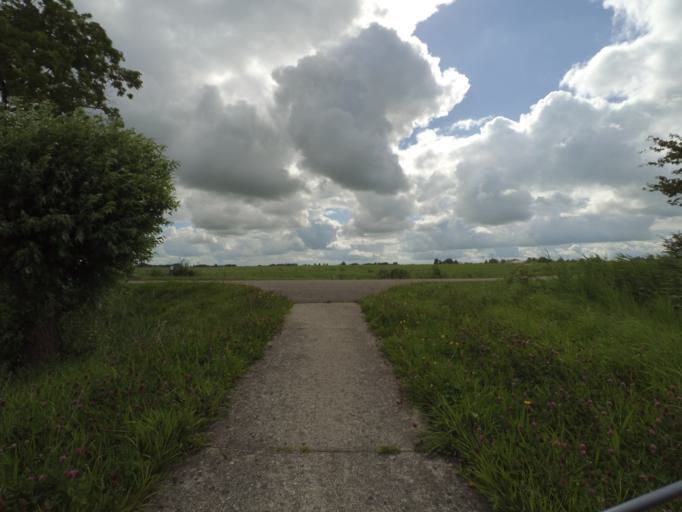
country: NL
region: Friesland
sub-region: Gemeente Kollumerland en Nieuwkruisland
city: Kollum
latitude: 53.2663
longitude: 6.1745
